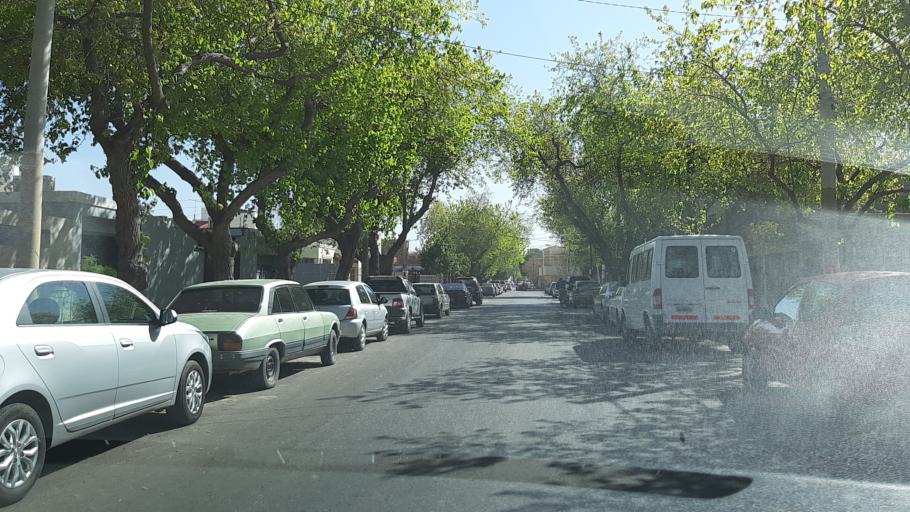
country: AR
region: San Juan
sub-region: Departamento de Santa Lucia
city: Santa Lucia
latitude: -31.5368
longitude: -68.5118
